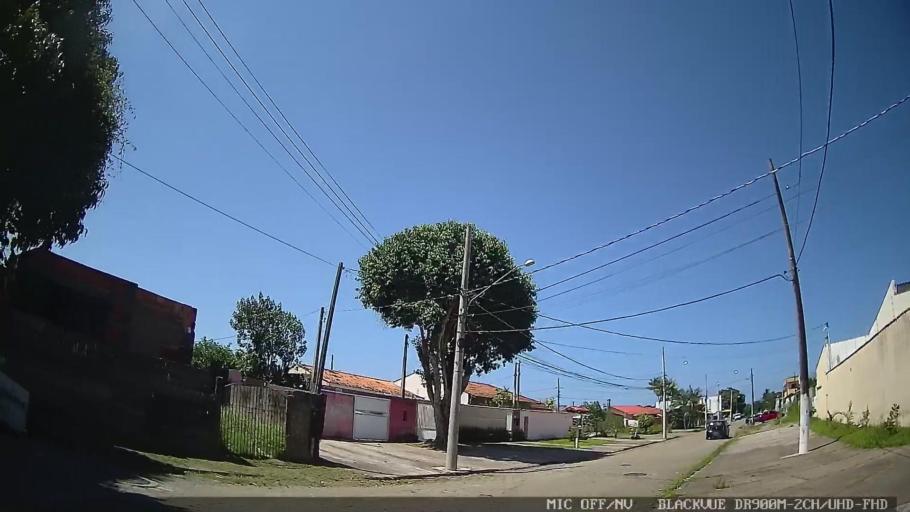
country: BR
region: Sao Paulo
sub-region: Peruibe
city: Peruibe
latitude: -24.3066
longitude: -46.9972
